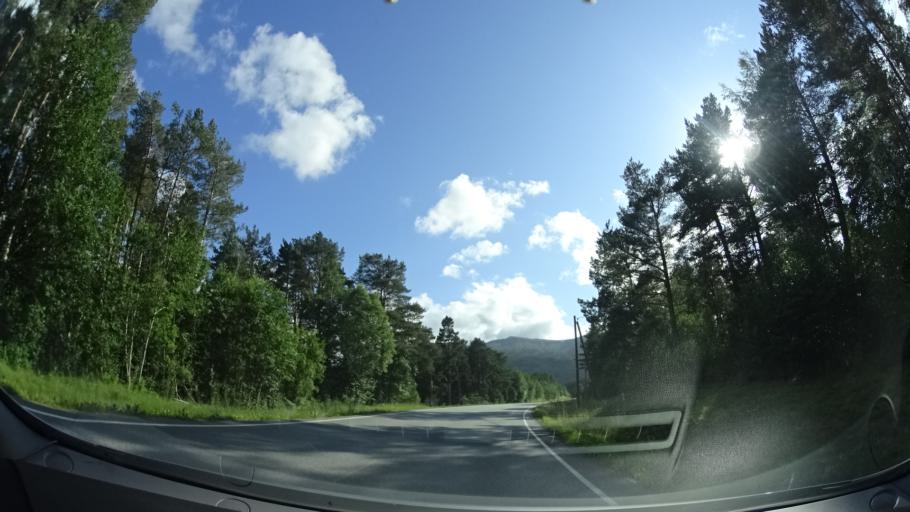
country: NO
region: More og Romsdal
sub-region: Aure
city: Aure
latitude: 63.1397
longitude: 8.5314
